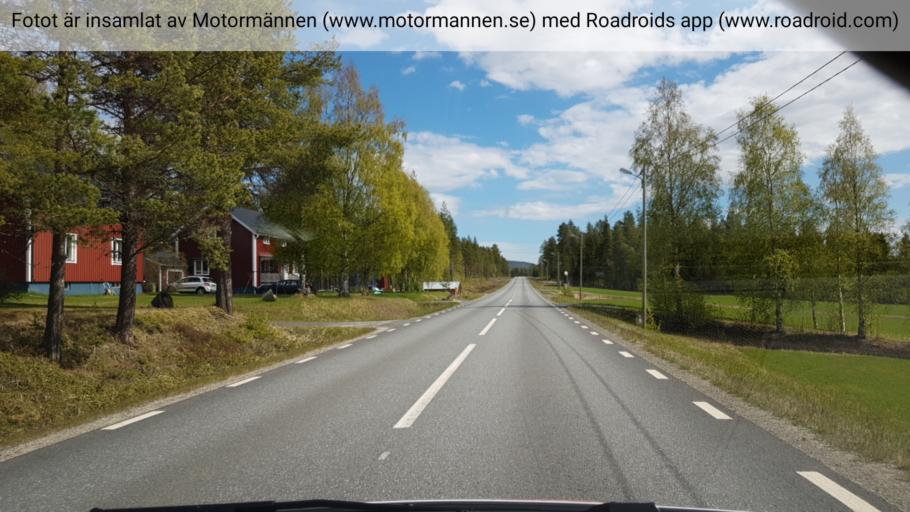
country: SE
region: Vaesterbotten
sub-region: Bjurholms Kommun
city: Bjurholm
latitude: 64.2885
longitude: 19.1983
